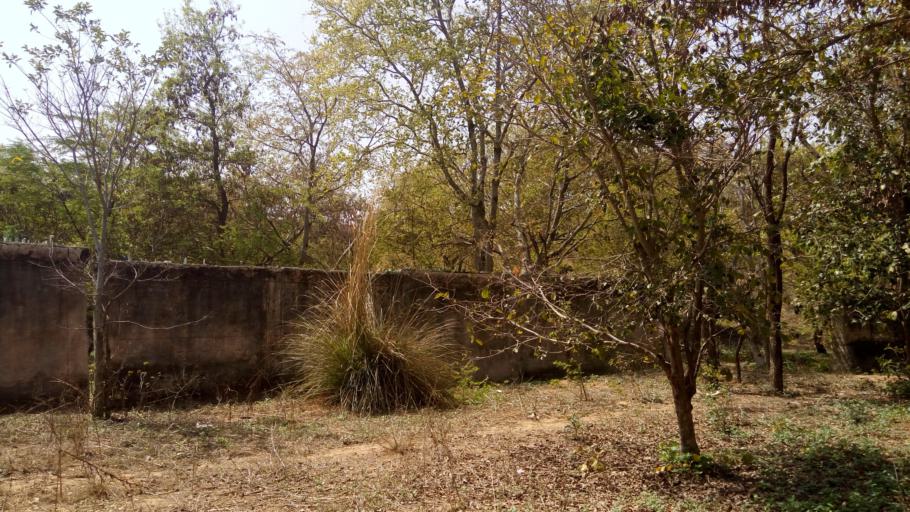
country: IN
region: Rajasthan
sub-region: Jaipur
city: Jaipur
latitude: 26.9381
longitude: 75.7836
